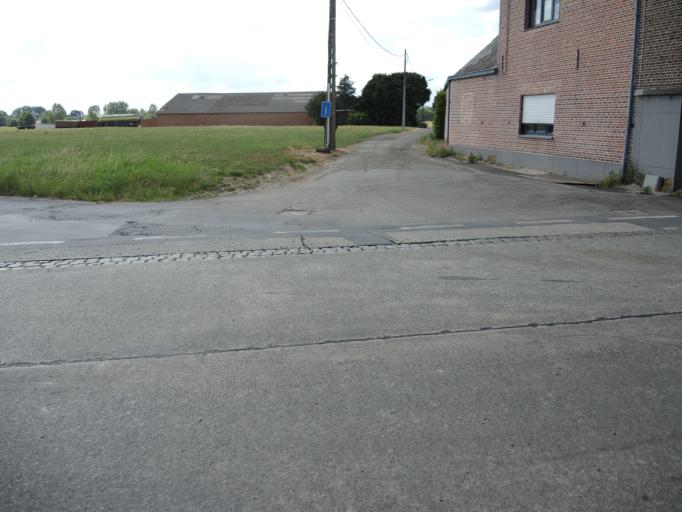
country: BE
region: Flanders
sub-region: Provincie Vlaams-Brabant
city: Londerzeel
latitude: 51.0342
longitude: 4.3237
